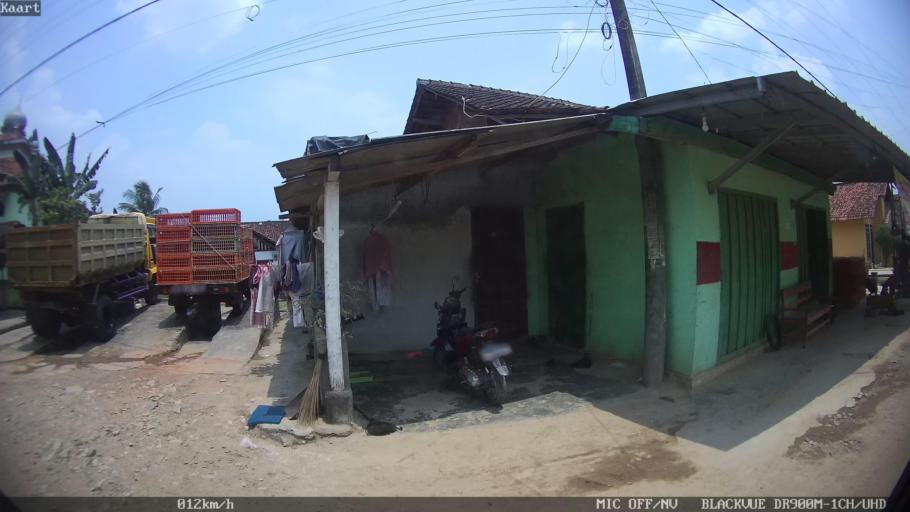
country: ID
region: Lampung
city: Pringsewu
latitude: -5.3649
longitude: 105.0015
